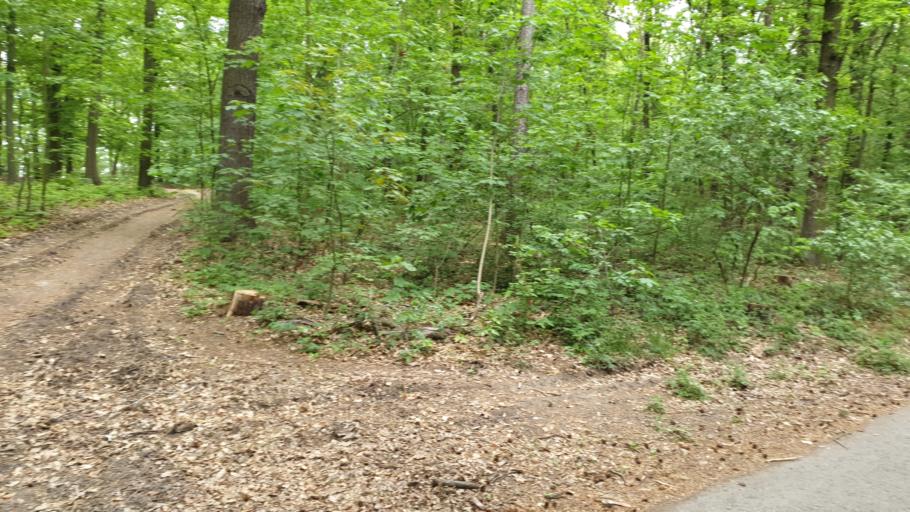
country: CZ
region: Central Bohemia
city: Horomerice
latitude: 50.1043
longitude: 14.3173
